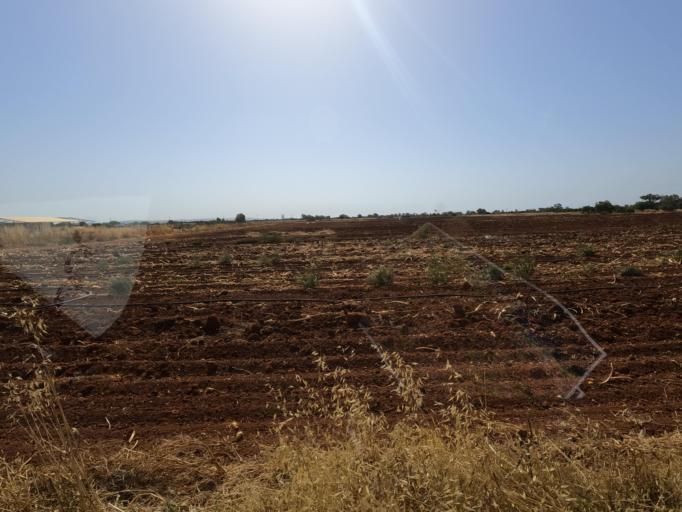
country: CY
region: Ammochostos
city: Liopetri
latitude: 34.9813
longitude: 33.8815
